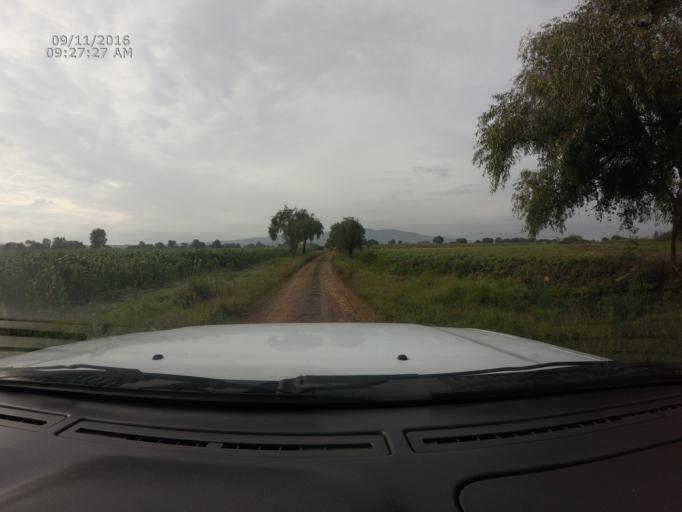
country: MX
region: Michoacan
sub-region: Morelia
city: La Mintzita (Piedra Dura)
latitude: 19.5902
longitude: -101.2911
